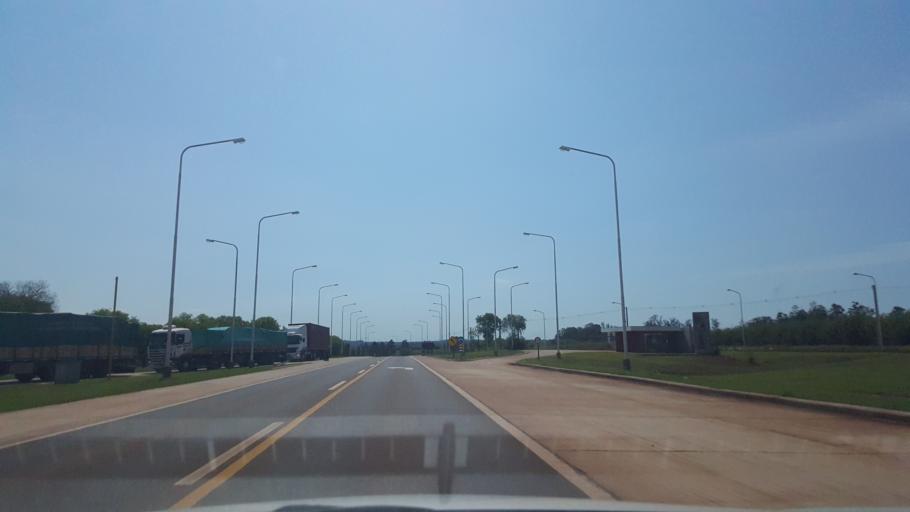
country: AR
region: Misiones
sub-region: Departamento de Apostoles
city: San Jose
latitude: -27.7816
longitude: -55.8168
